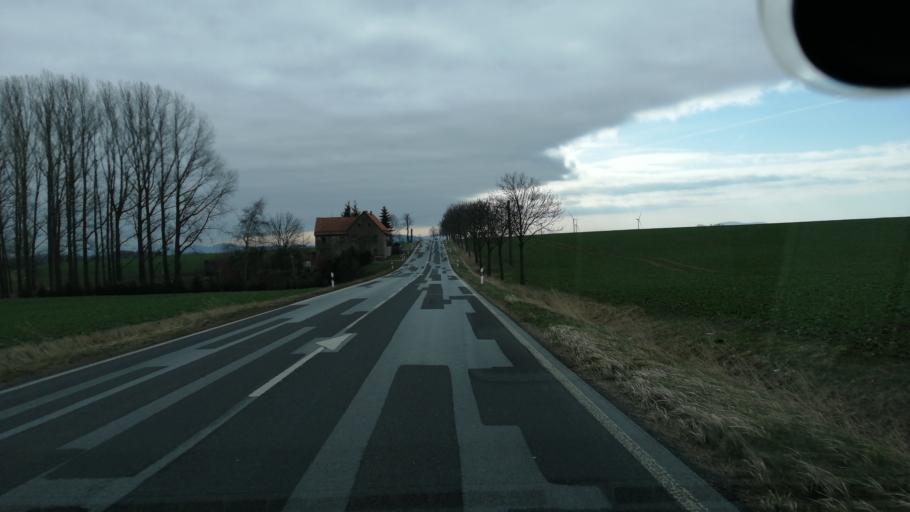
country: DE
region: Saxony
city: Herrnhut
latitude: 51.0388
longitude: 14.7104
